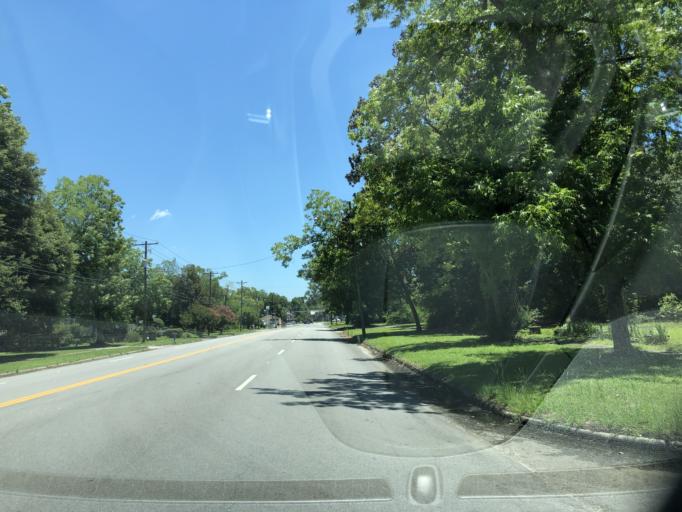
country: US
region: South Carolina
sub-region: Orangeburg County
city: Branchville
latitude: 33.2503
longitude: -80.8193
